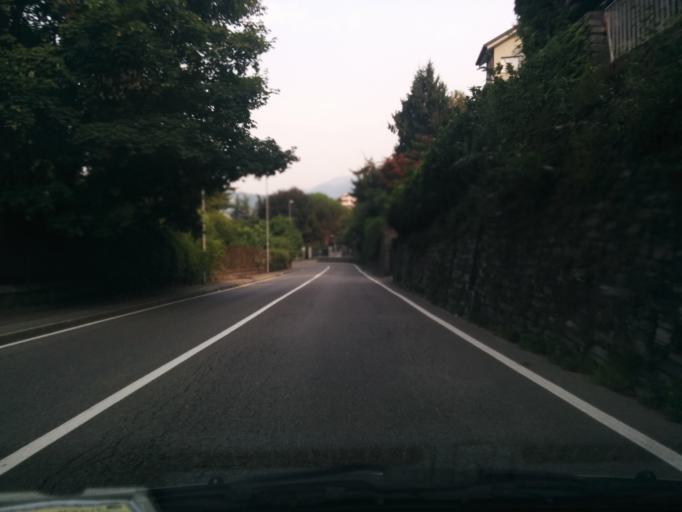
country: IT
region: Lombardy
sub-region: Provincia di Como
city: Brunate
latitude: 45.8037
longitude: 9.1022
